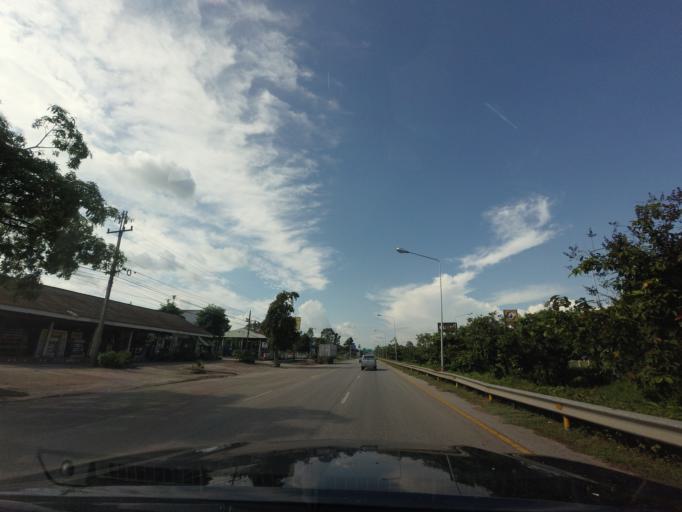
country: TH
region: Nong Khai
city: Sa Khrai
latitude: 17.7625
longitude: 102.7695
